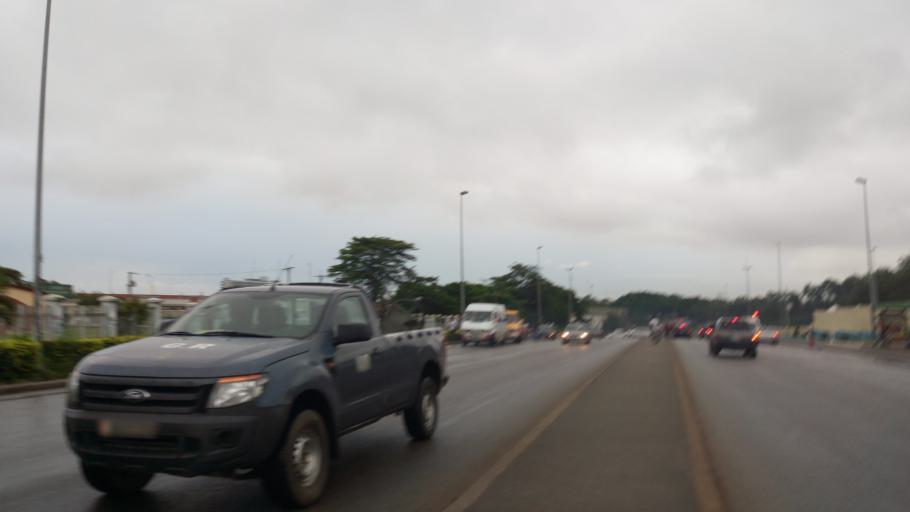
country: CI
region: Lagunes
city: Abidjan
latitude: 5.3505
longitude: -3.9877
